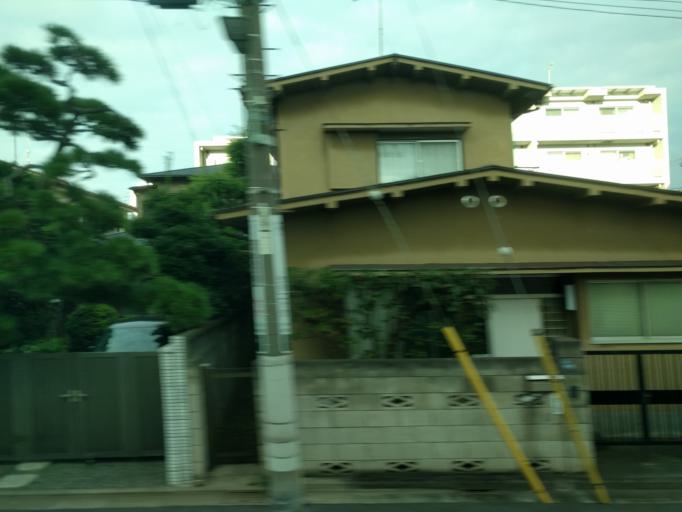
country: JP
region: Kanagawa
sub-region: Kawasaki-shi
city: Kawasaki
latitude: 35.5874
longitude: 139.6815
